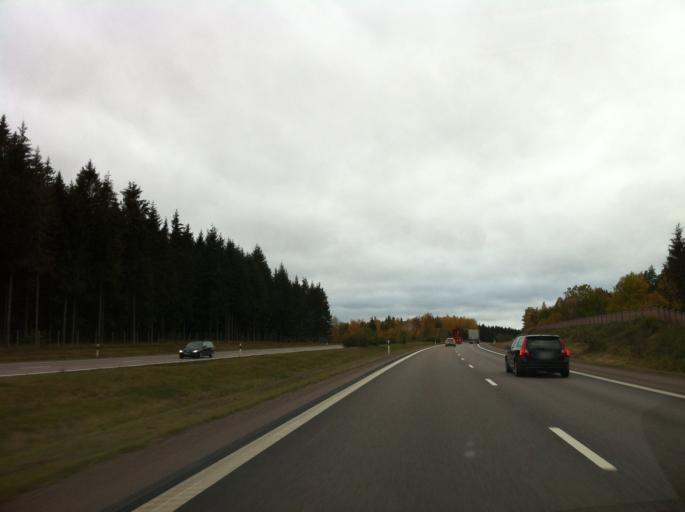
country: SE
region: OEstergoetland
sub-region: Boxholms Kommun
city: Boxholm
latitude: 58.3069
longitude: 15.0011
